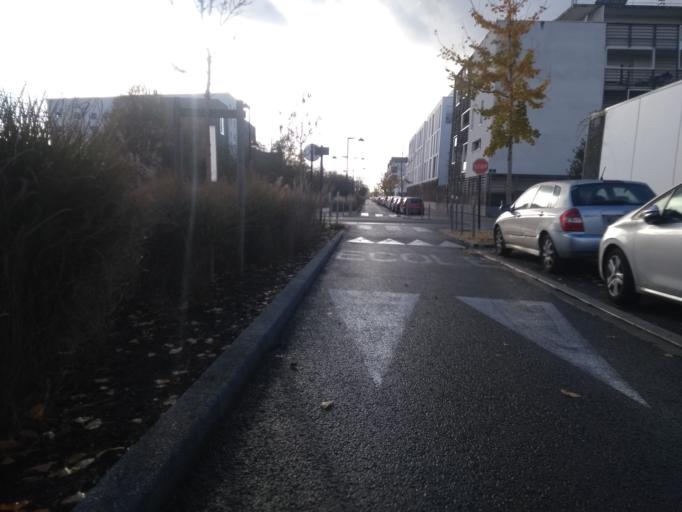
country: FR
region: Aquitaine
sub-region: Departement de la Gironde
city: Floirac
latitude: 44.8274
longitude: -0.5288
